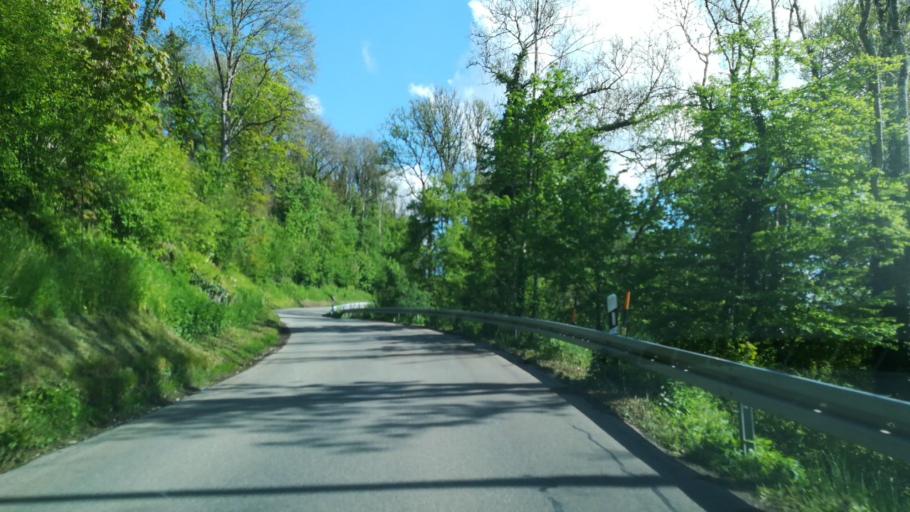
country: DE
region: Baden-Wuerttemberg
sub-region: Freiburg Region
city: Stuhlingen
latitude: 47.7419
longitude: 8.4365
